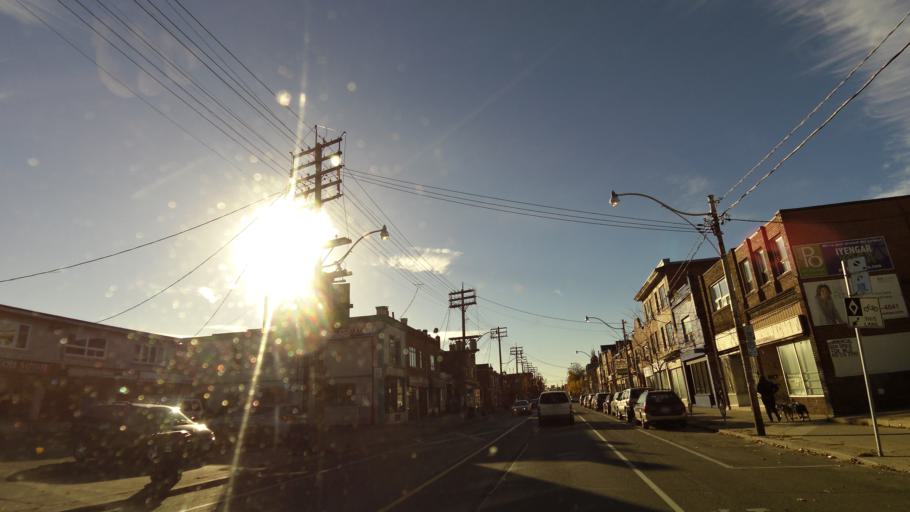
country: CA
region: Ontario
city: Toronto
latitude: 43.6655
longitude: -79.4528
